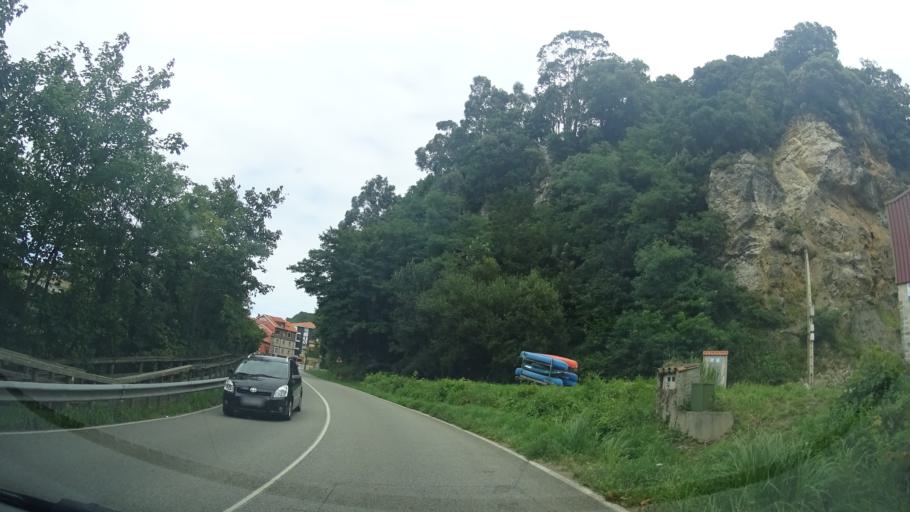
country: ES
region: Asturias
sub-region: Province of Asturias
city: Ribadesella
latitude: 43.4628
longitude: -5.0681
